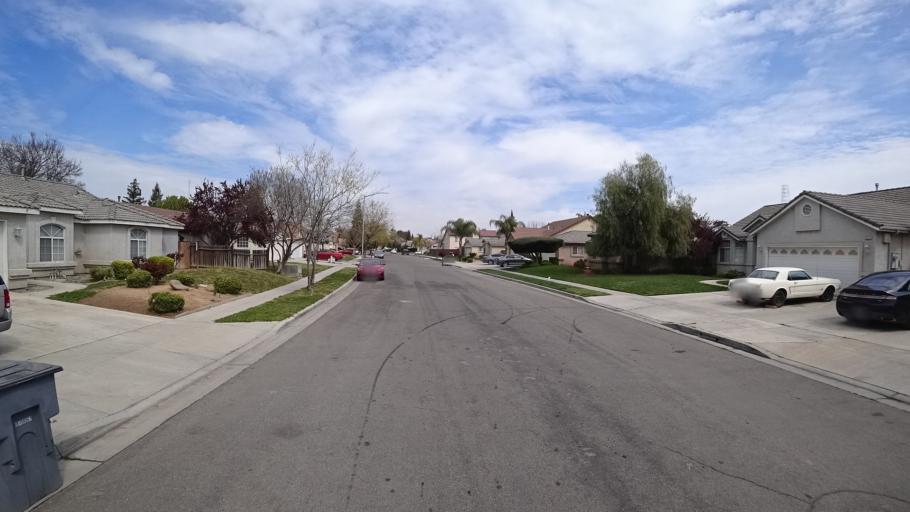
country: US
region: California
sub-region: Fresno County
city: West Park
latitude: 36.8163
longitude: -119.8863
